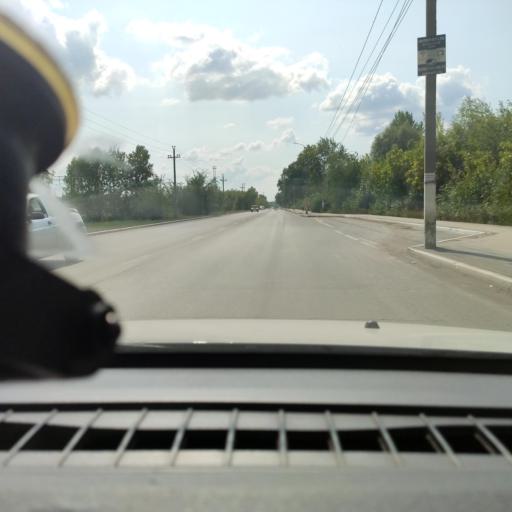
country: RU
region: Samara
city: Chapayevsk
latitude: 52.9835
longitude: 49.7077
